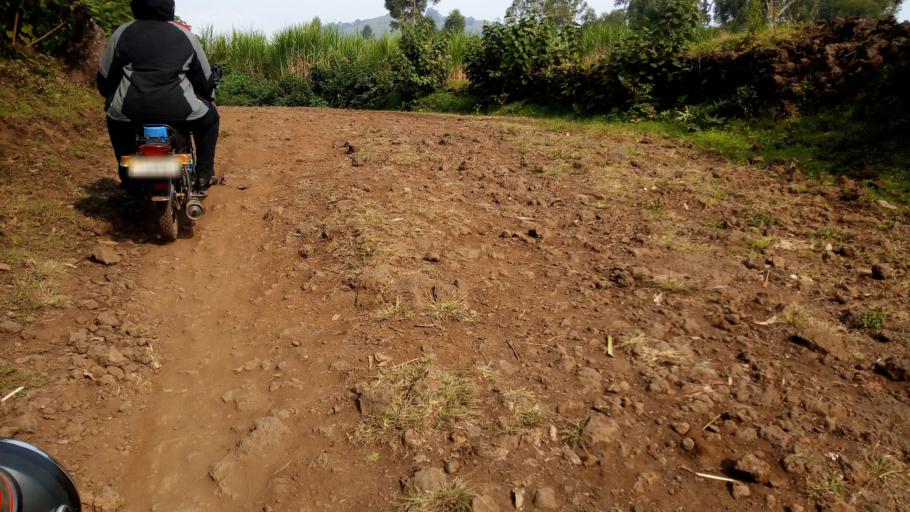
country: UG
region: Western Region
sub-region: Kisoro District
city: Kisoro
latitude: -1.3108
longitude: 29.6553
